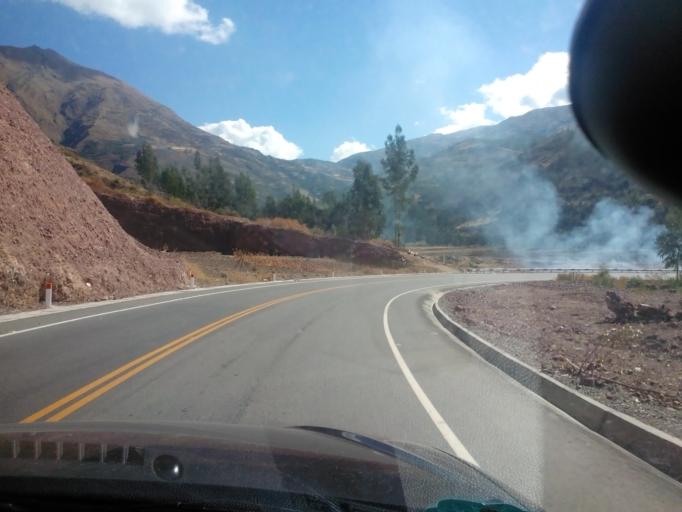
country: PE
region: Cusco
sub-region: Provincia de Quispicanchis
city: Huaro
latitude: -13.6743
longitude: -71.6326
